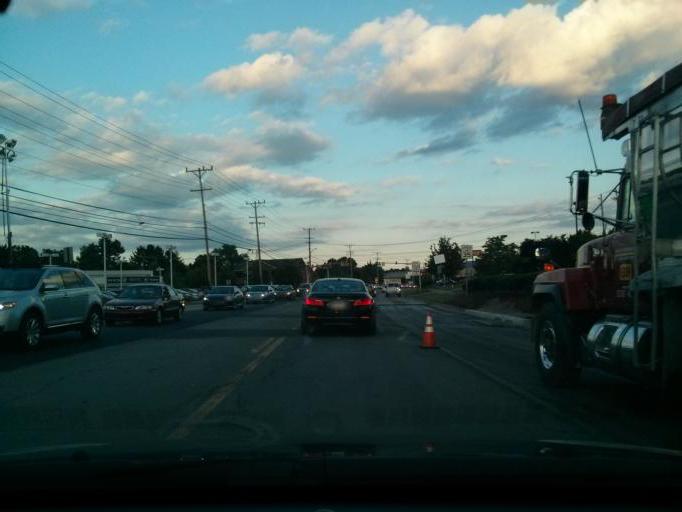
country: US
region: Pennsylvania
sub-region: Centre County
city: Park Forest Village
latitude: 40.8077
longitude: -77.8930
